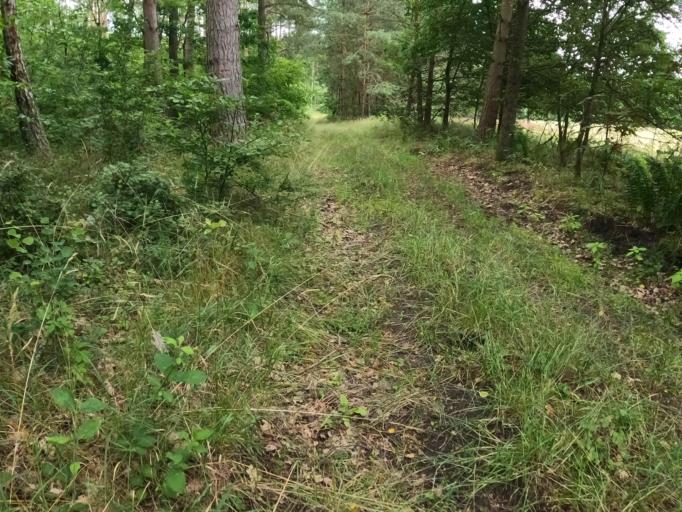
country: PL
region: West Pomeranian Voivodeship
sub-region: Powiat bialogardzki
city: Karlino
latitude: 53.9967
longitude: 15.9119
